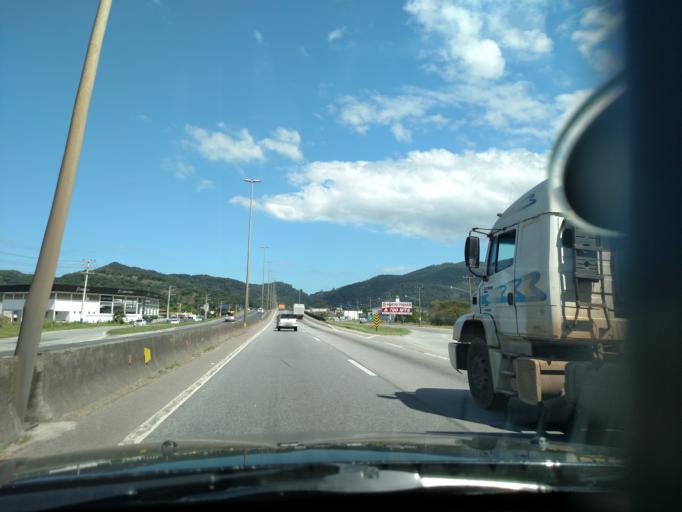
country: BR
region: Santa Catarina
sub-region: Balneario Camboriu
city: Balneario Camboriu
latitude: -27.0165
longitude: -48.6115
